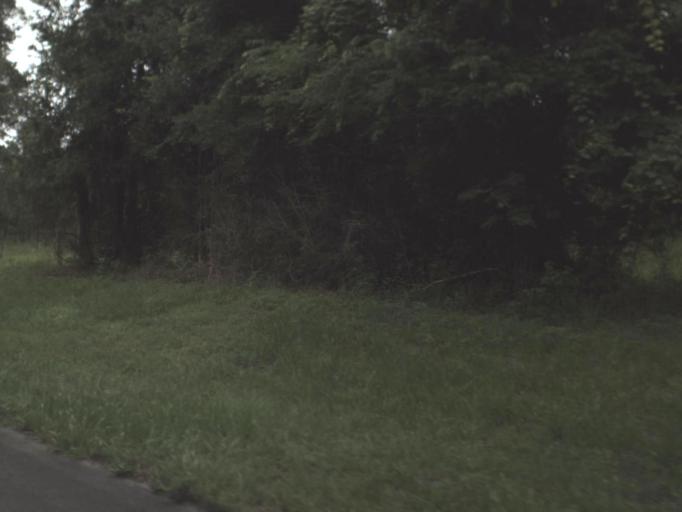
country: US
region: Florida
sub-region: Alachua County
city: Archer
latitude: 29.4915
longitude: -82.4936
